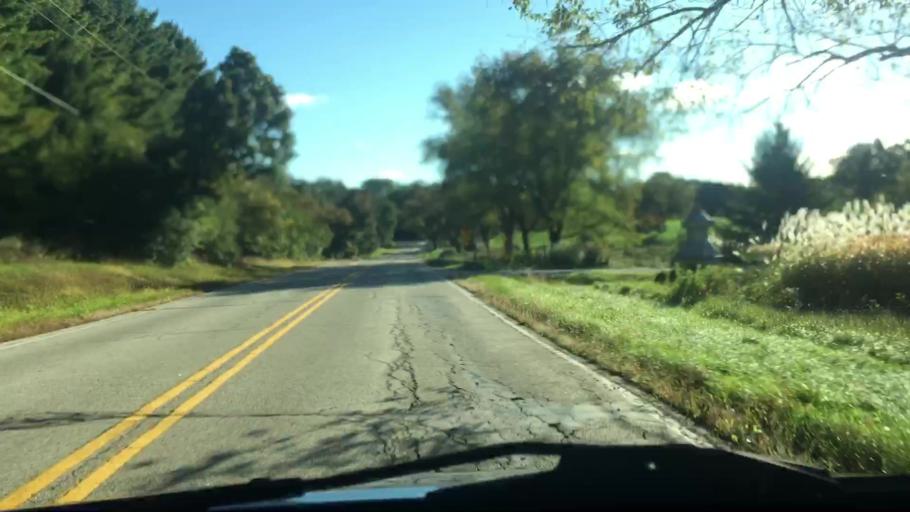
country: US
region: Wisconsin
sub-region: Waukesha County
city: North Prairie
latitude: 42.9445
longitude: -88.4163
